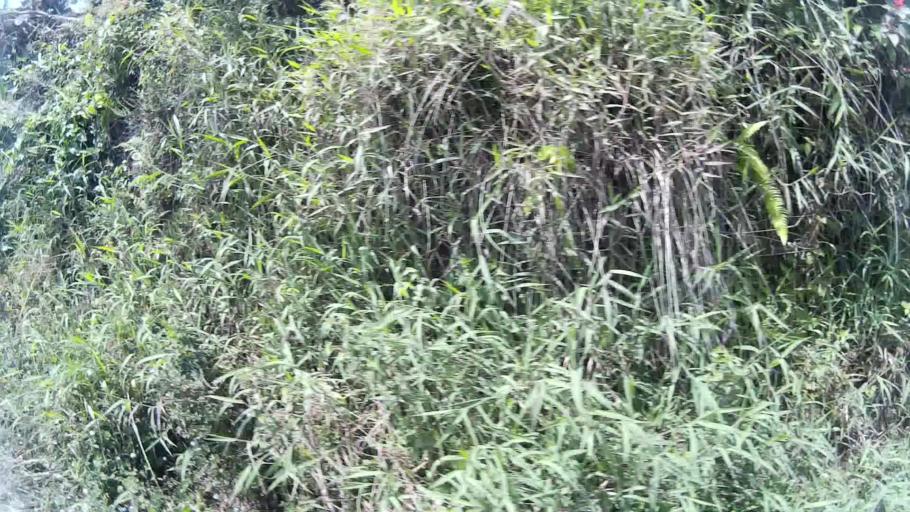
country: CO
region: Caldas
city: Belalcazar
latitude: 4.9737
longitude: -75.8198
